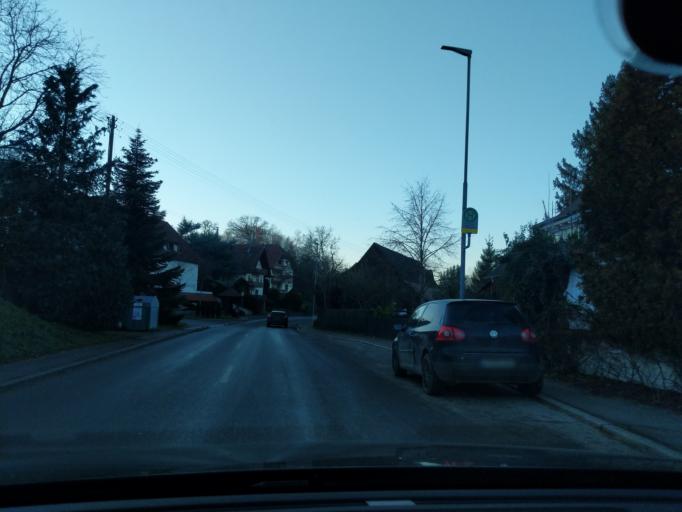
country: DE
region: Baden-Wuerttemberg
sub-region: Tuebingen Region
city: Salem
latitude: 47.7453
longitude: 9.3022
